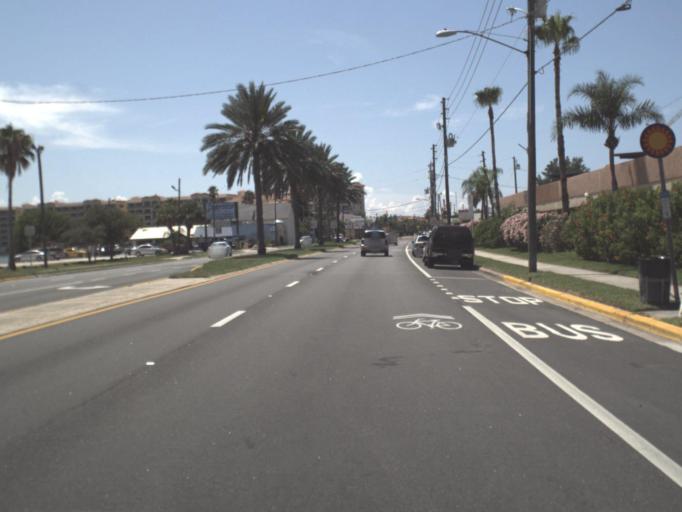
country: US
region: Florida
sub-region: Pinellas County
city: Redington Shores
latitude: 27.8306
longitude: -82.8316
